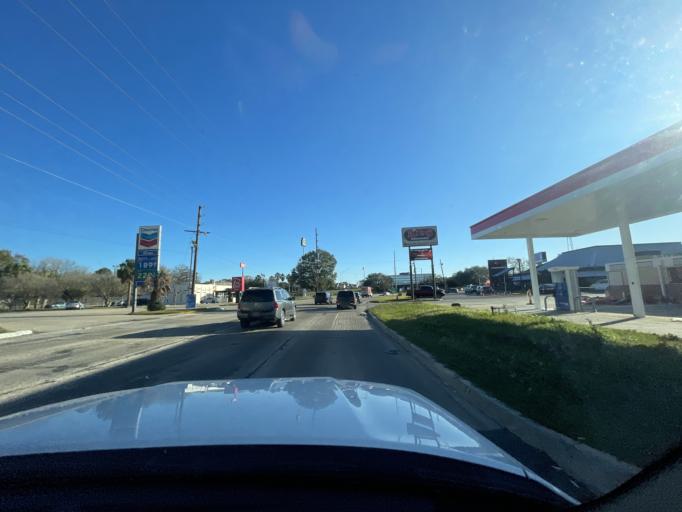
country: US
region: Louisiana
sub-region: East Baton Rouge Parish
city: Baton Rouge
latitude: 30.4263
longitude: -91.1507
